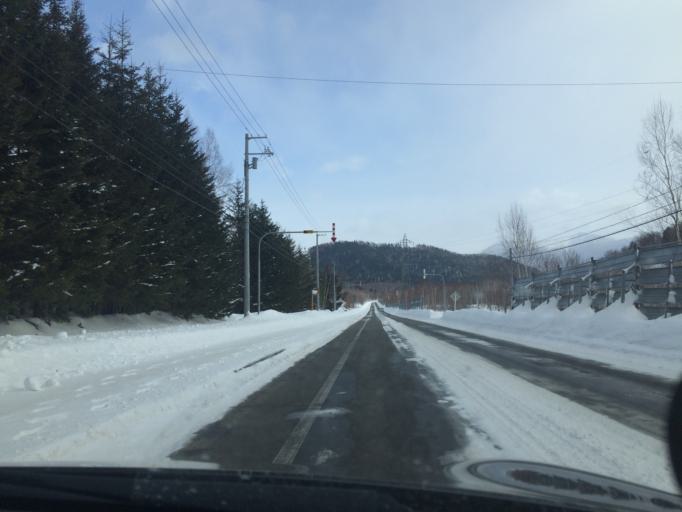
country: JP
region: Hokkaido
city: Shimo-furano
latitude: 43.0551
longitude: 142.6308
